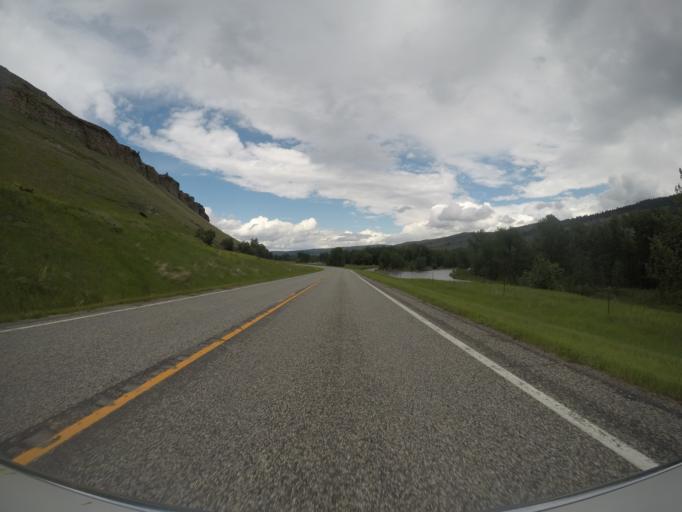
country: US
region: Montana
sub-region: Sweet Grass County
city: Big Timber
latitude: 45.5852
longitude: -110.1845
